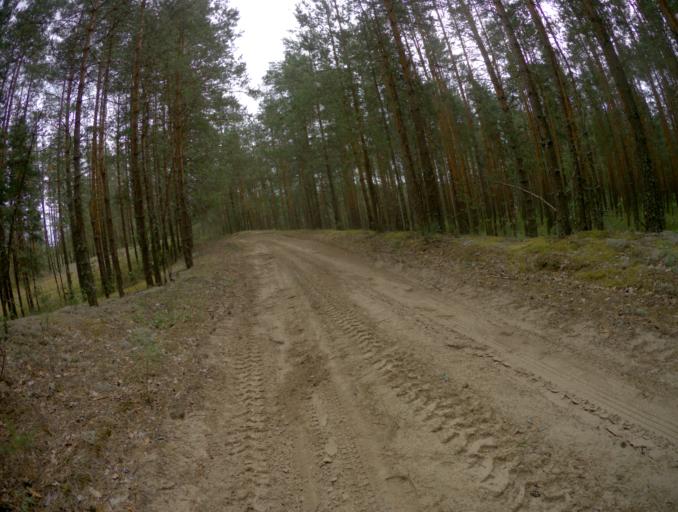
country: RU
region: Nizjnij Novgorod
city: Frolishchi
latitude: 56.3179
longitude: 42.6808
